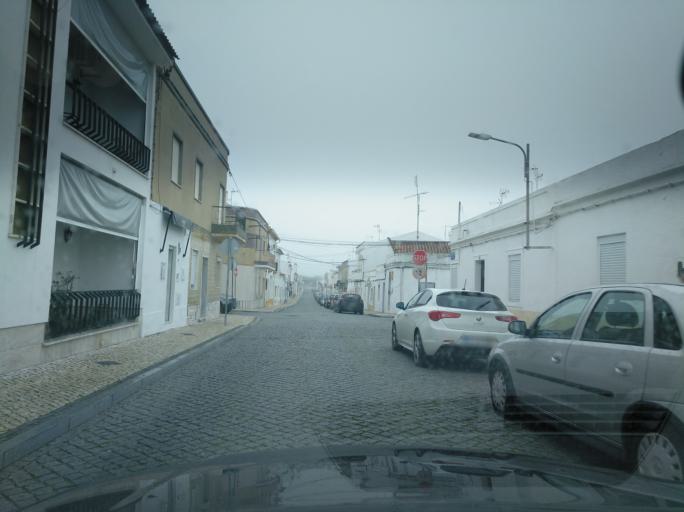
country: PT
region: Portalegre
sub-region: Campo Maior
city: Campo Maior
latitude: 39.0153
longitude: -7.0660
